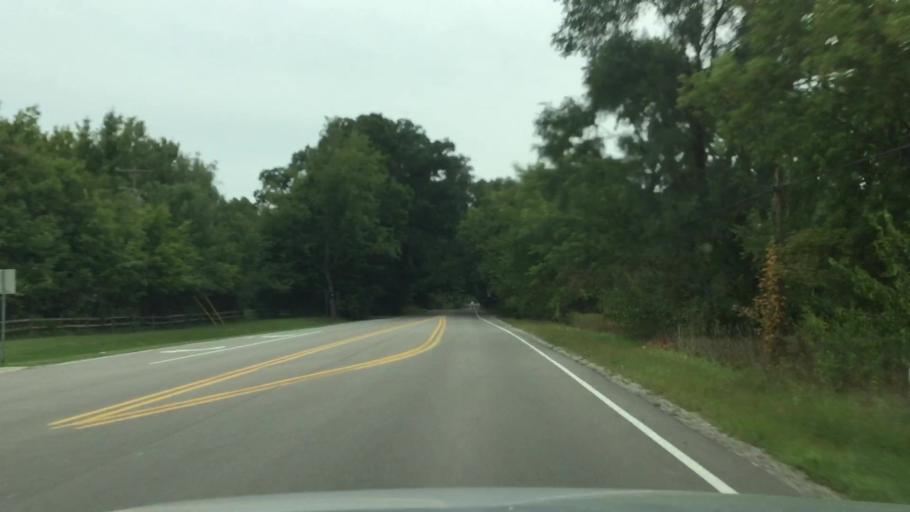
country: US
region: Michigan
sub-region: Washtenaw County
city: Ypsilanti
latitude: 42.1779
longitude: -83.6409
